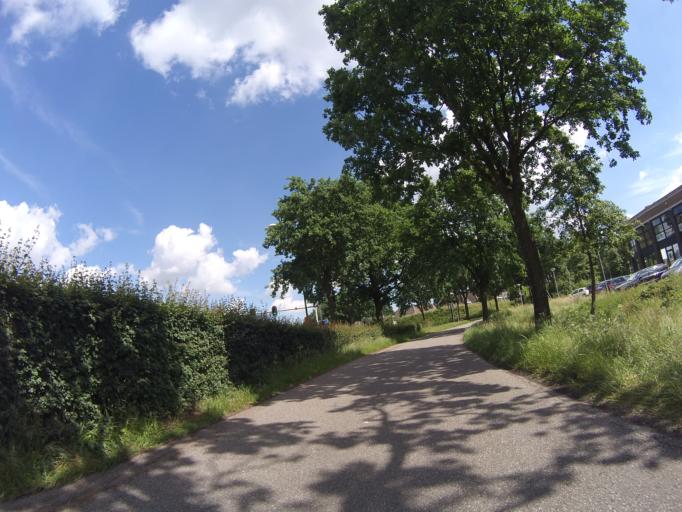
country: NL
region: Utrecht
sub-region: Gemeente Amersfoort
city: Hoogland
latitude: 52.1810
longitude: 5.3701
